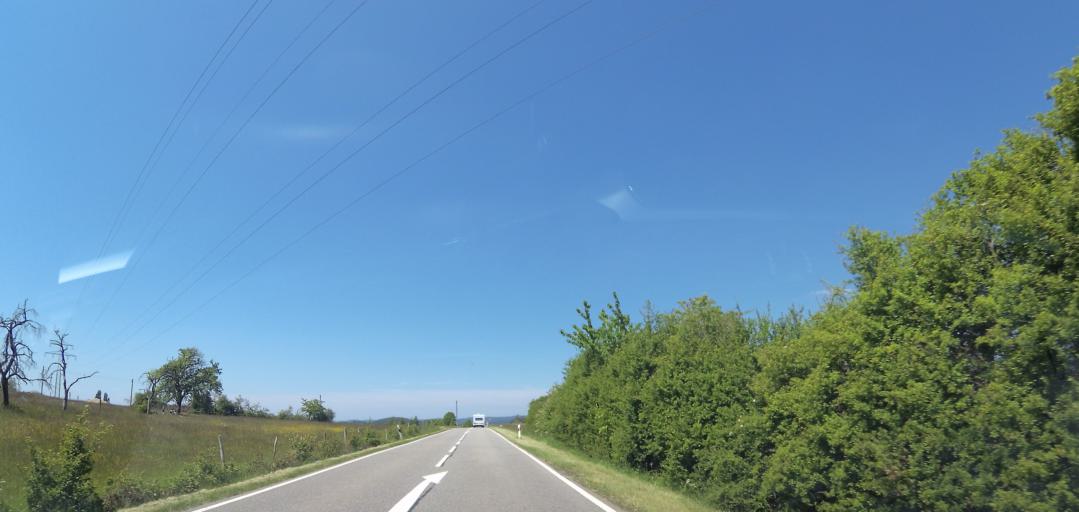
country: DE
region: Saarland
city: Losheim
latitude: 49.4640
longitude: 6.7061
